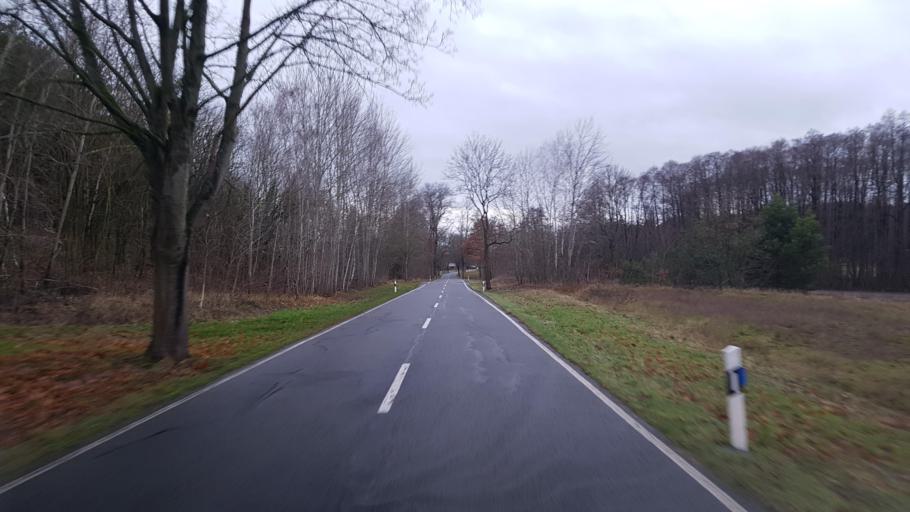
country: DE
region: Brandenburg
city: Wendisch Rietz
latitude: 52.0680
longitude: 14.0372
